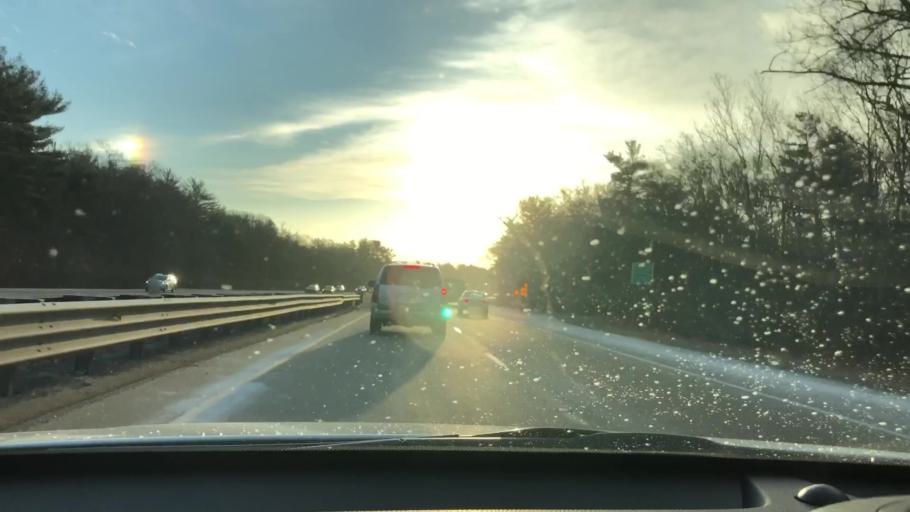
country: US
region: Massachusetts
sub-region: Norfolk County
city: Weymouth
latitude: 42.1825
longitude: -70.9215
